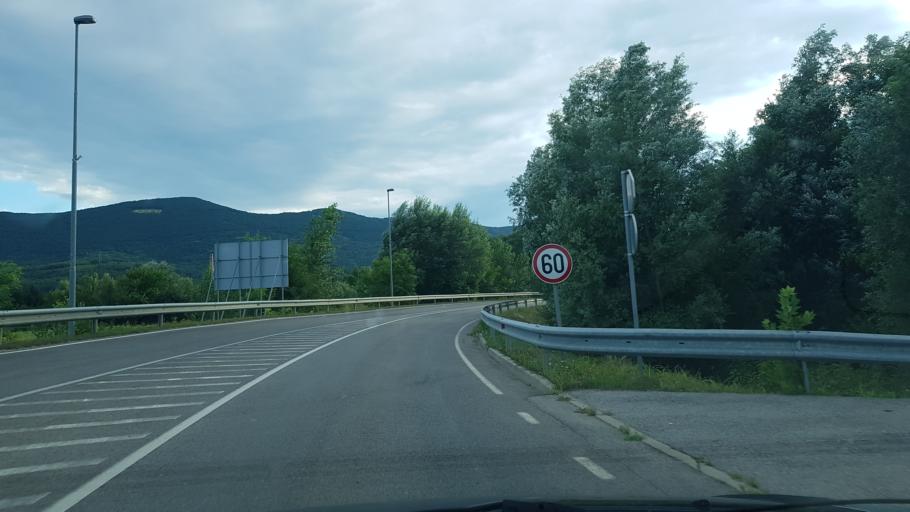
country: SI
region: Rence-Vogrsko
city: Rence
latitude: 45.8915
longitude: 13.6660
